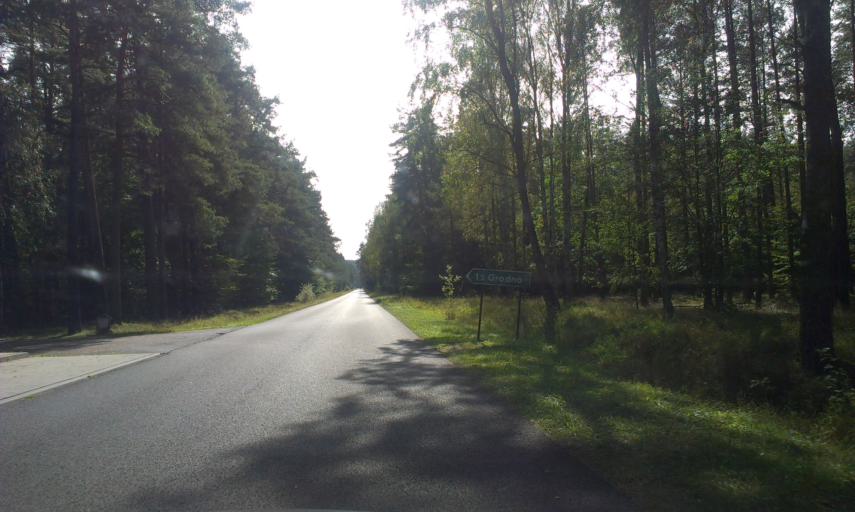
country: PL
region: Greater Poland Voivodeship
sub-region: Powiat zlotowski
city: Okonek
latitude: 53.5022
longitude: 16.9798
